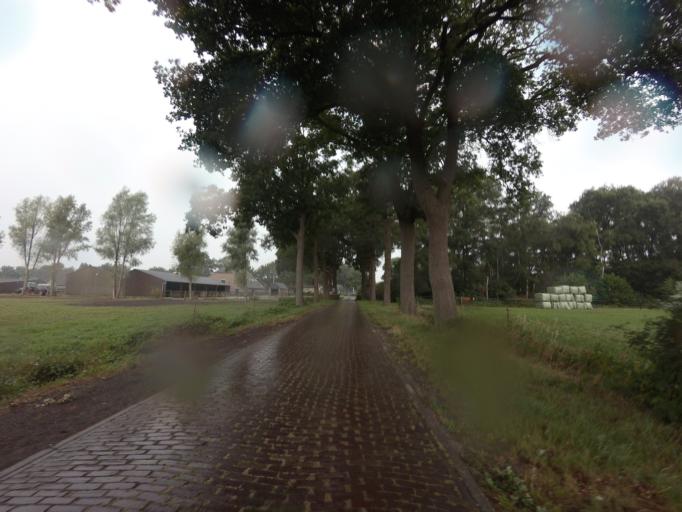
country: NL
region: Drenthe
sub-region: Gemeente Hoogeveen
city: Hoogeveen
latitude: 52.6678
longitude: 6.5076
